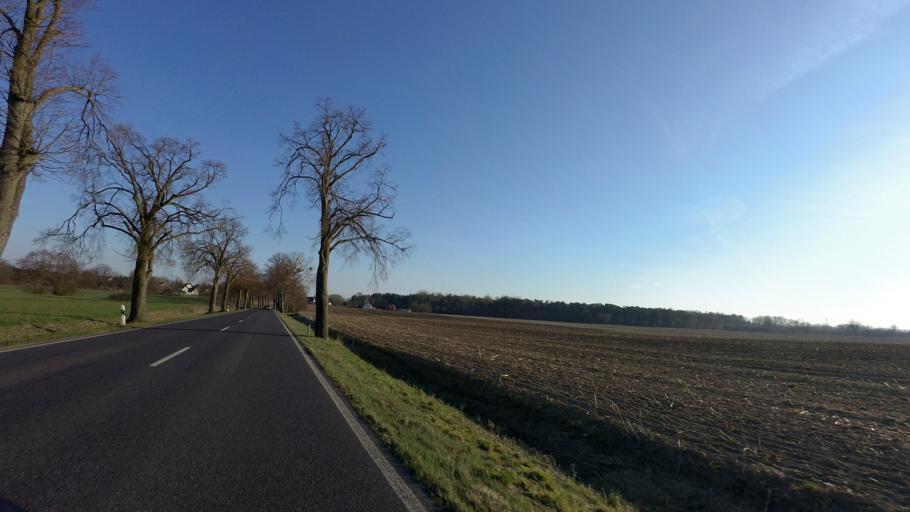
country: DE
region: Brandenburg
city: Britz
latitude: 52.8936
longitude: 13.8044
